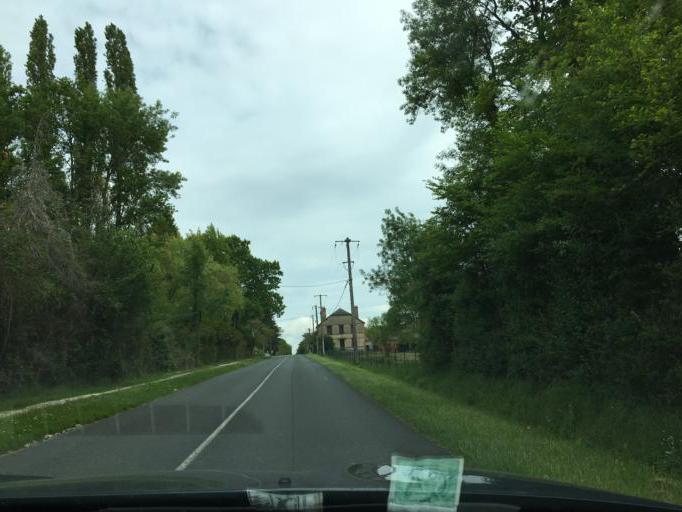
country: FR
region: Centre
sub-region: Departement du Loir-et-Cher
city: Dhuizon
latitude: 47.6618
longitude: 1.6696
